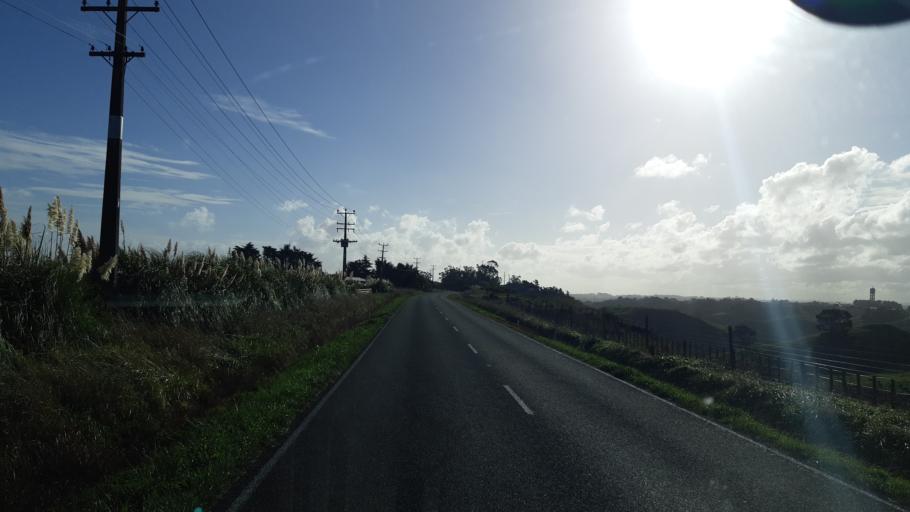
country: NZ
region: Manawatu-Wanganui
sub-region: Wanganui District
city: Wanganui
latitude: -39.9418
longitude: 175.0871
